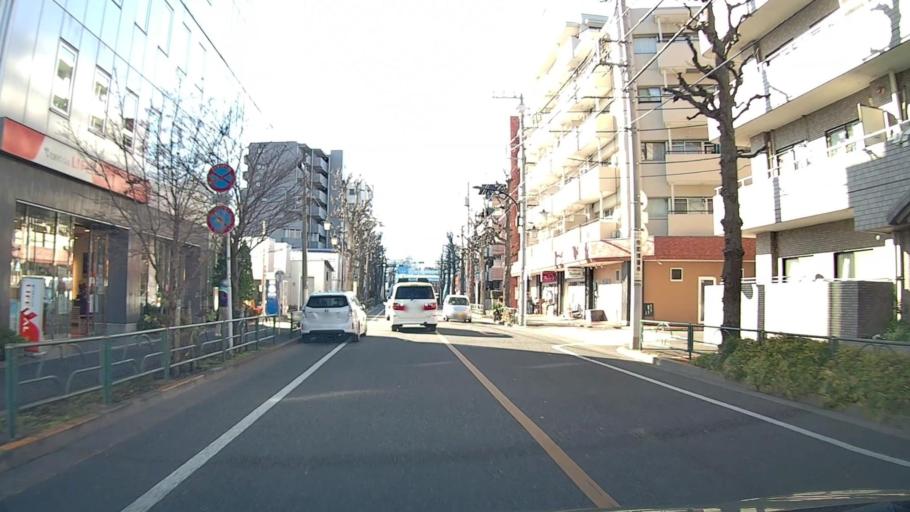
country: JP
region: Tokyo
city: Tokyo
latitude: 35.7231
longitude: 139.6589
